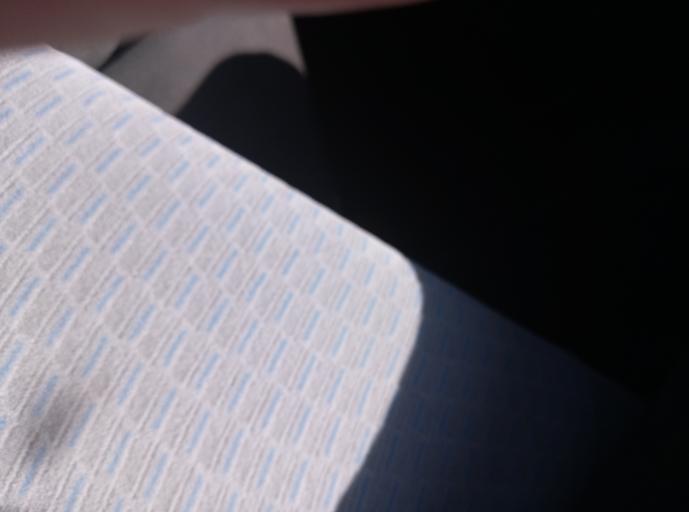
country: CD
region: Nord Kivu
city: Goma
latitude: -1.6454
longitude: 29.1689
